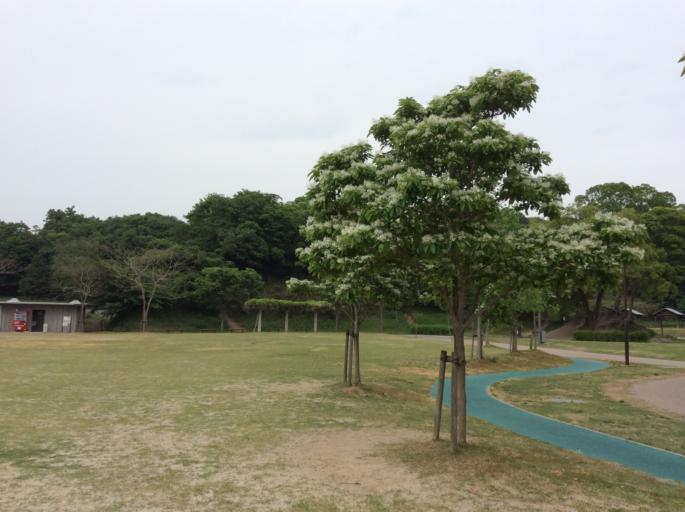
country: JP
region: Shizuoka
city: Kakegawa
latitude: 34.7753
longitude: 138.0610
